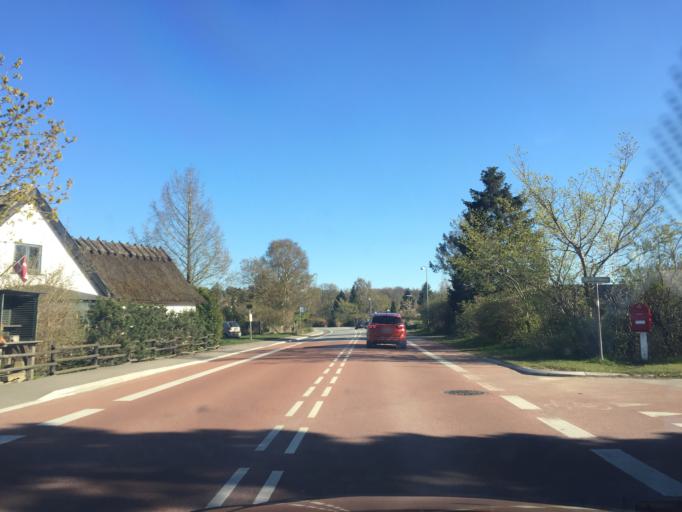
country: DK
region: Capital Region
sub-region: Halsnaes Kommune
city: Frederiksvaerk
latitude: 56.0024
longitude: 12.0120
